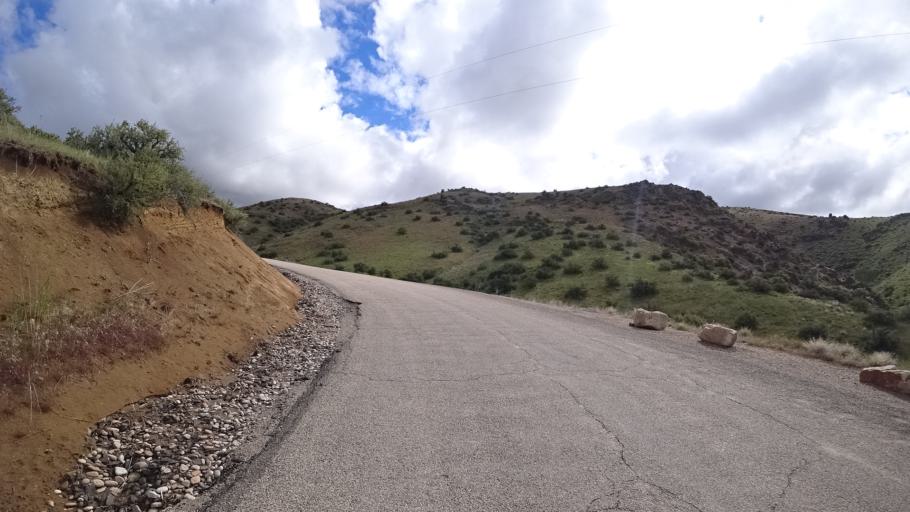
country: US
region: Idaho
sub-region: Ada County
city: Garden City
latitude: 43.7313
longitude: -116.2303
